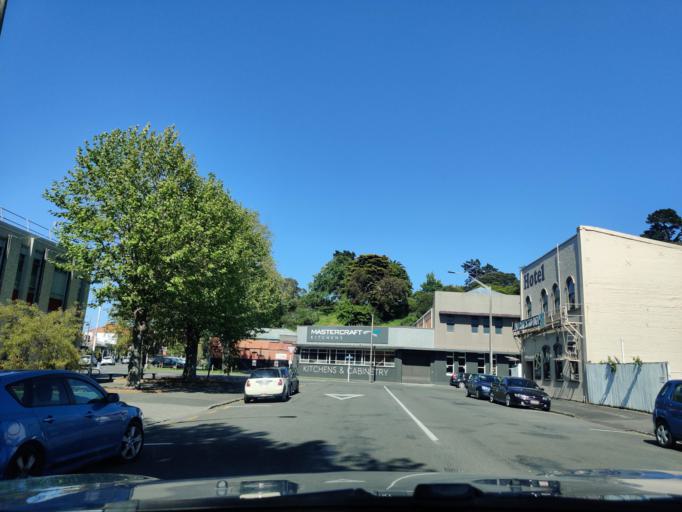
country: NZ
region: Manawatu-Wanganui
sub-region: Wanganui District
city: Wanganui
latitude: -39.9314
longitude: 175.0562
